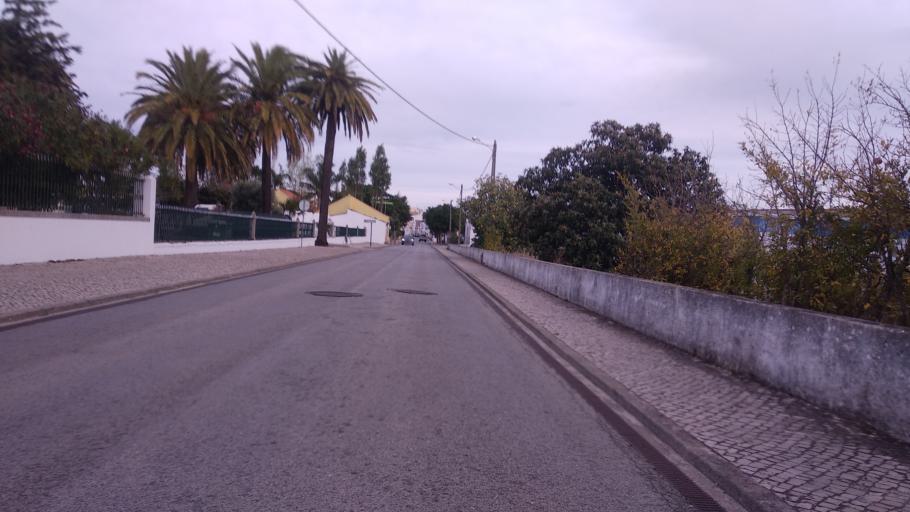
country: PT
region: Faro
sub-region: Sao Bras de Alportel
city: Sao Bras de Alportel
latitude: 37.1532
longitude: -7.8950
